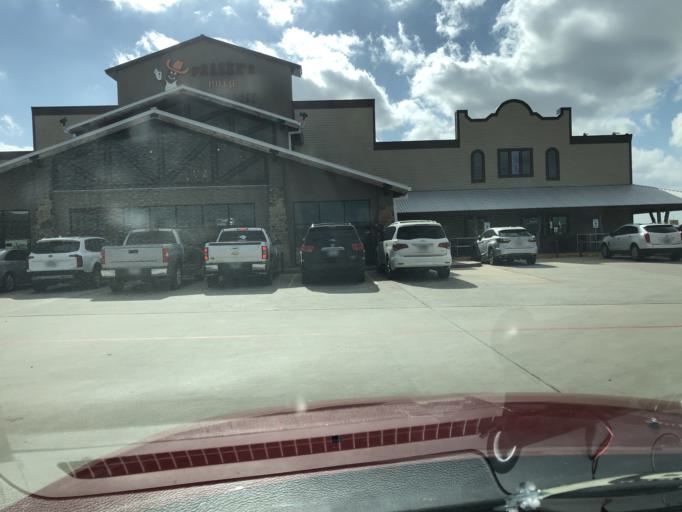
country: US
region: Texas
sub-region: Austin County
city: Sealy
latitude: 29.7625
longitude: -96.1872
